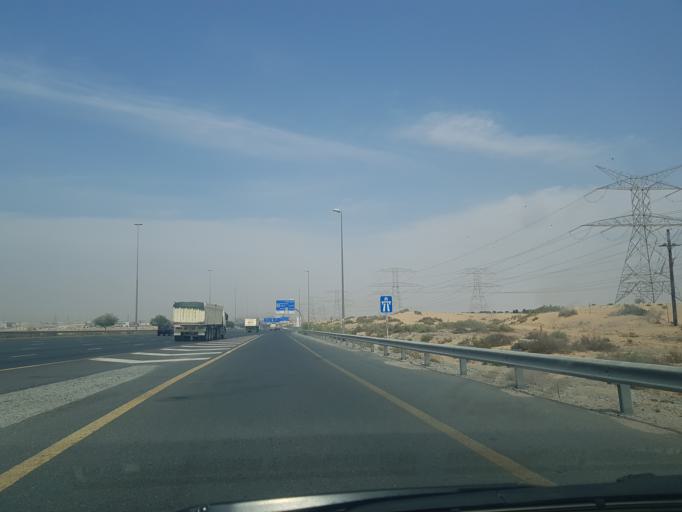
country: AE
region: Ash Shariqah
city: Sharjah
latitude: 25.2109
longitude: 55.5528
